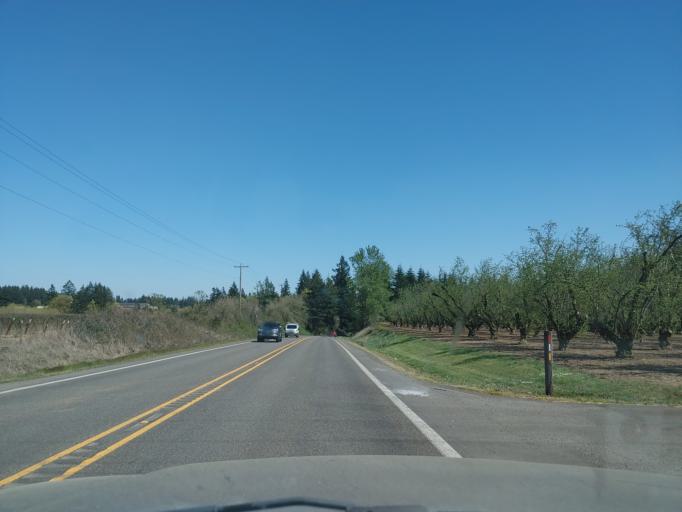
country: US
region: Oregon
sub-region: Yamhill County
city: Newberg
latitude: 45.2342
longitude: -122.8981
